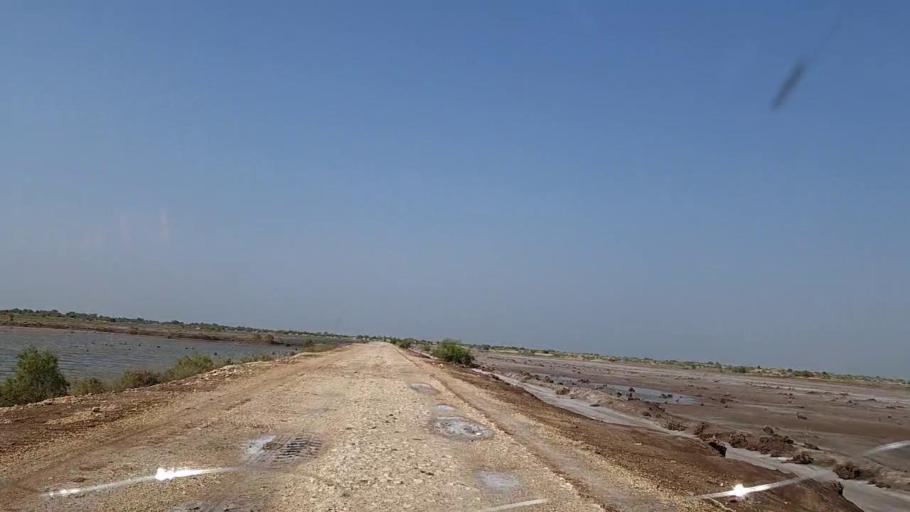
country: PK
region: Sindh
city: Khanpur
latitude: 27.6903
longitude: 69.3822
